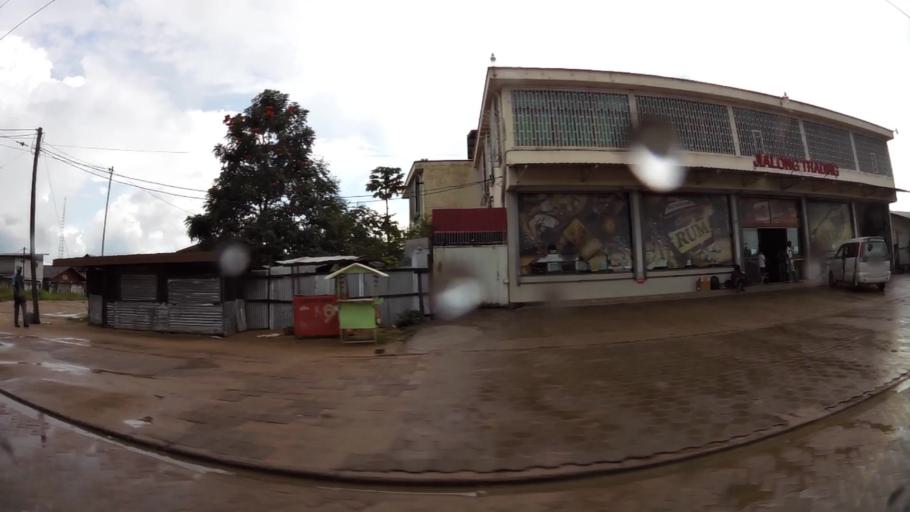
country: SR
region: Paramaribo
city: Paramaribo
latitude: 5.8130
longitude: -55.1733
